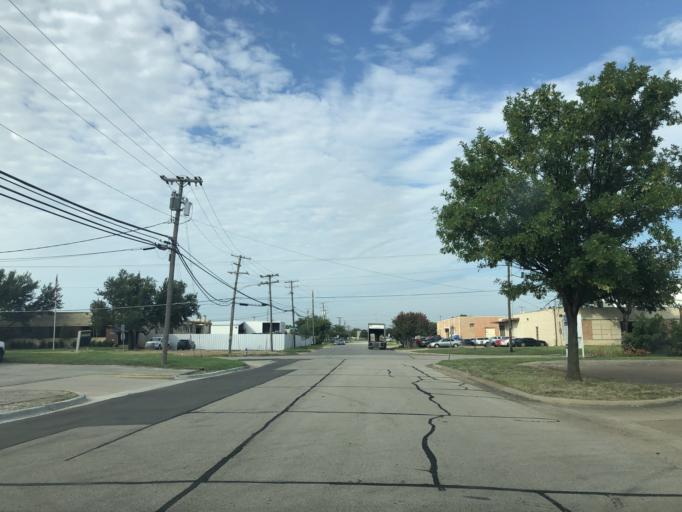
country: US
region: Texas
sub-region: Dallas County
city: Irving
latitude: 32.8180
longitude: -96.8822
